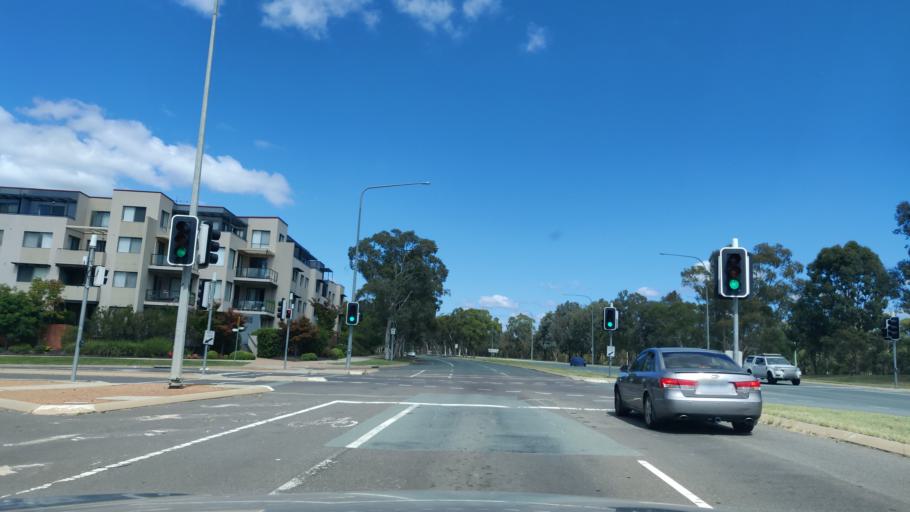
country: AU
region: Australian Capital Territory
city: Macarthur
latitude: -35.4117
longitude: 149.0618
